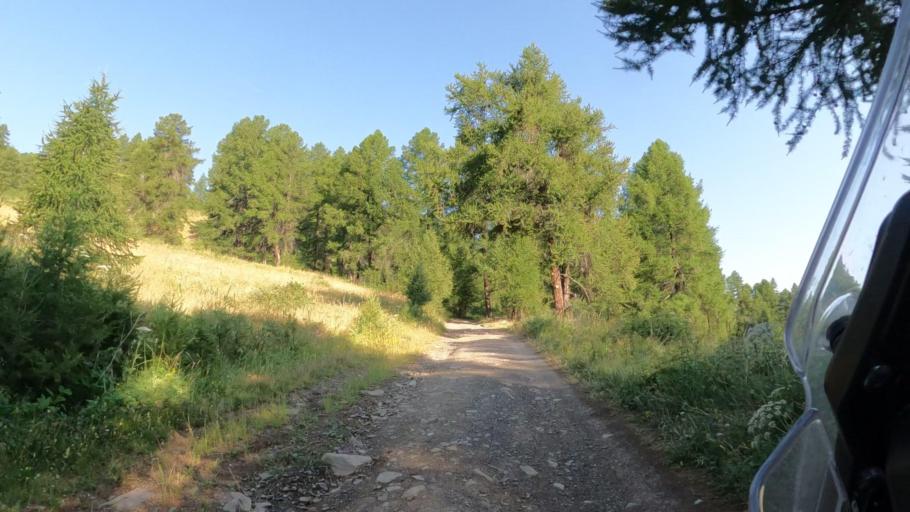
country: FR
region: Provence-Alpes-Cote d'Azur
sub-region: Departement des Hautes-Alpes
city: Guillestre
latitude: 44.6090
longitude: 6.6703
